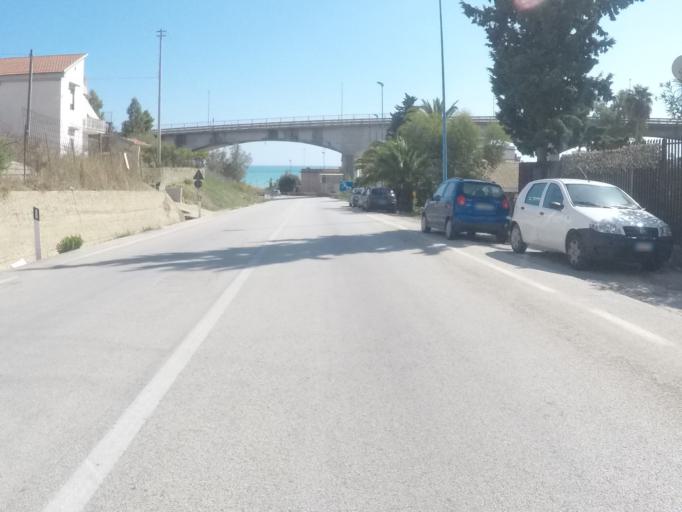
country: IT
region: Sicily
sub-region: Agrigento
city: Porto Empedocle
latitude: 37.2953
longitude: 13.5015
